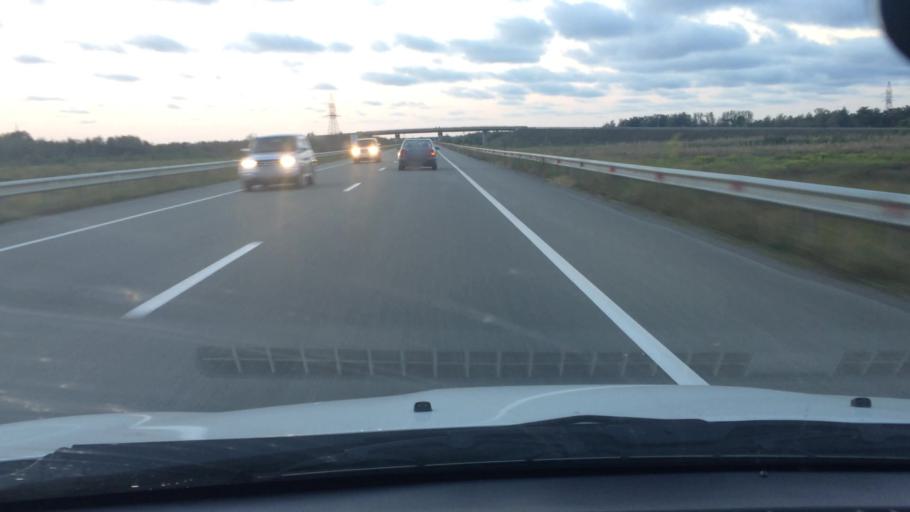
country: GE
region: Ajaria
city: Ochkhamuri
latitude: 41.8894
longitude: 41.8086
